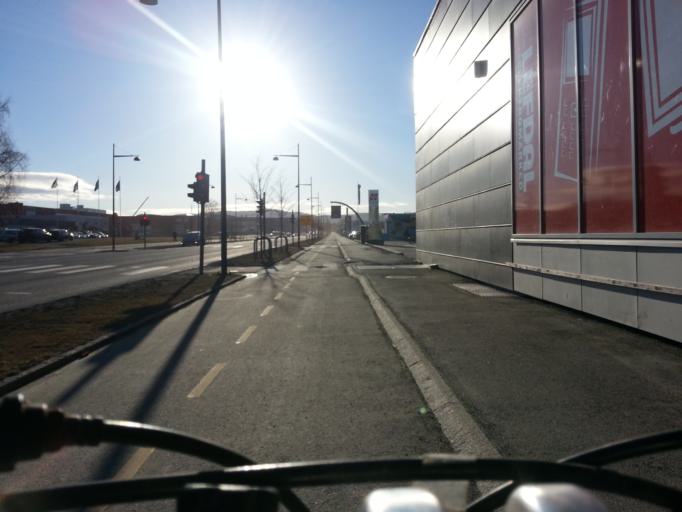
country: NO
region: Sor-Trondelag
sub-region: Trondheim
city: Trondheim
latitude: 63.4433
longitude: 10.4510
